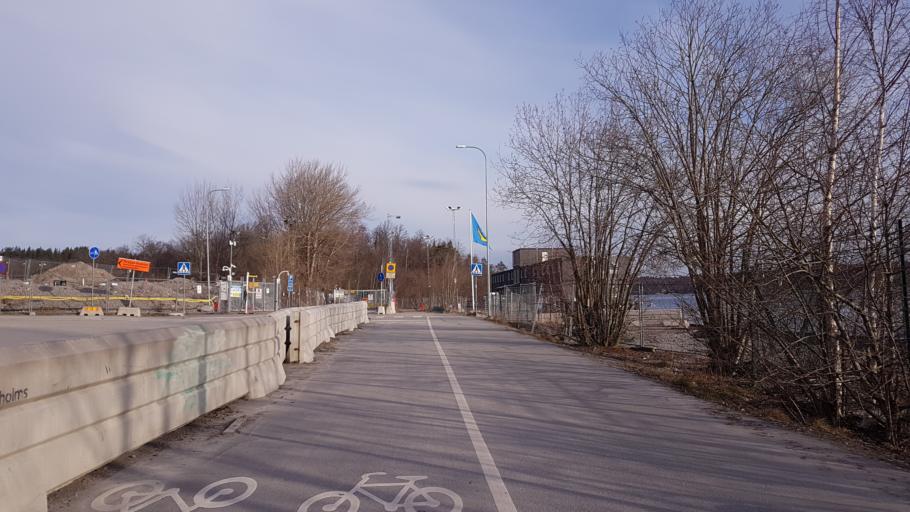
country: SE
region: Stockholm
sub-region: Stockholms Kommun
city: OEstermalm
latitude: 59.3598
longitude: 18.0994
